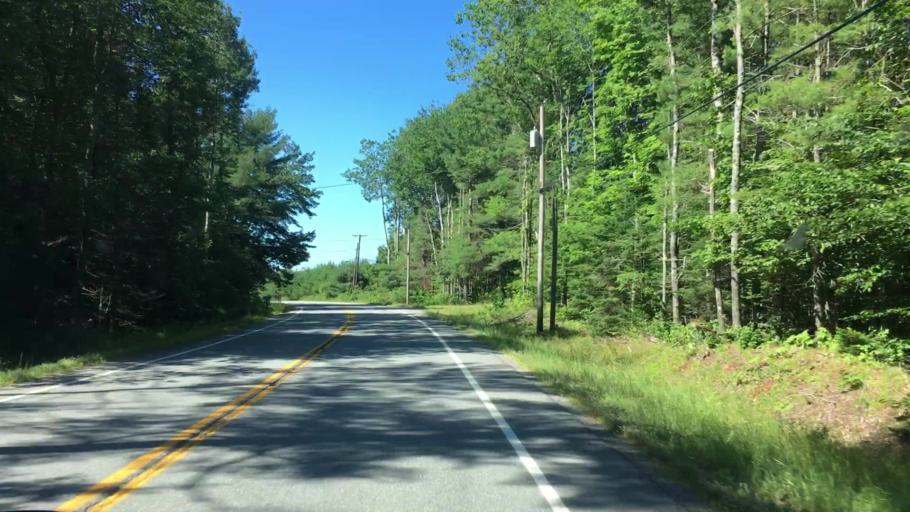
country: US
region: Maine
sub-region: Hancock County
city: Dedham
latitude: 44.6750
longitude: -68.6711
